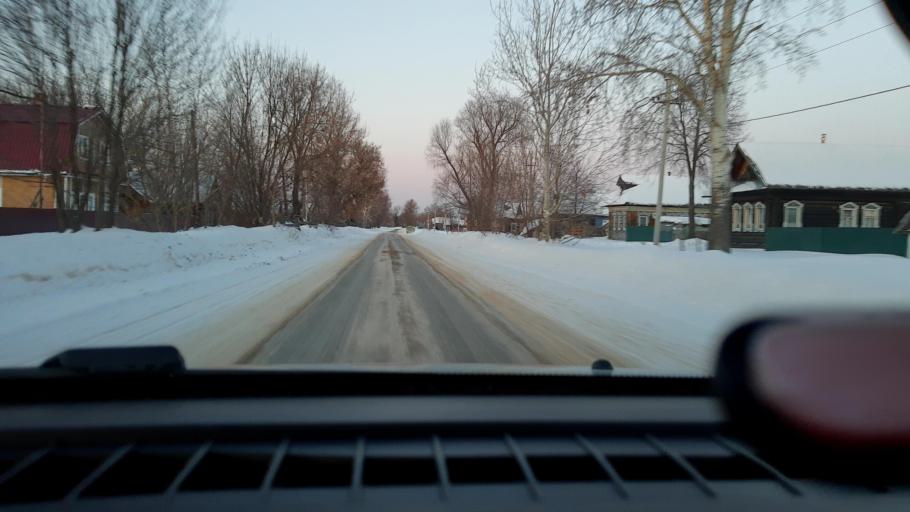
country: RU
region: Nizjnij Novgorod
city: Lyskovo
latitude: 56.1199
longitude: 45.3646
